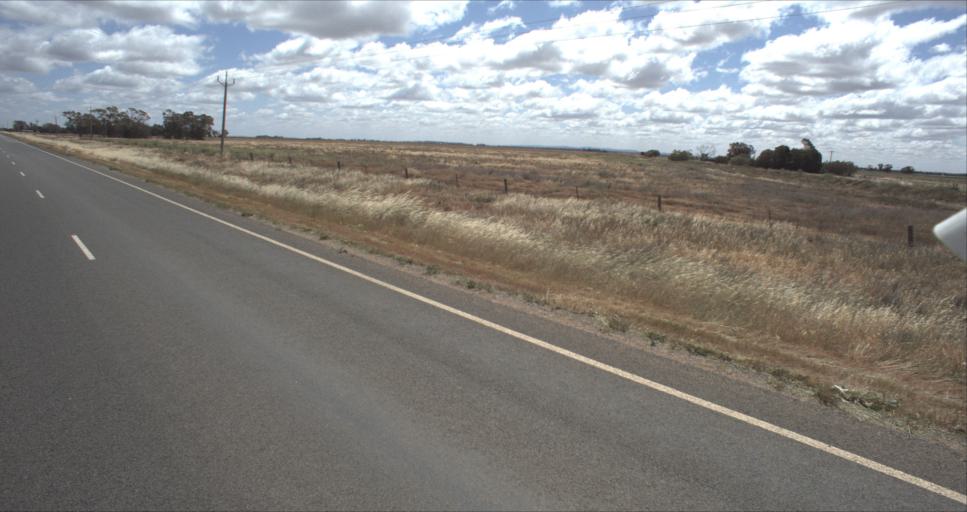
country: AU
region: New South Wales
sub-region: Murrumbidgee Shire
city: Darlington Point
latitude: -34.4867
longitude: 146.1604
